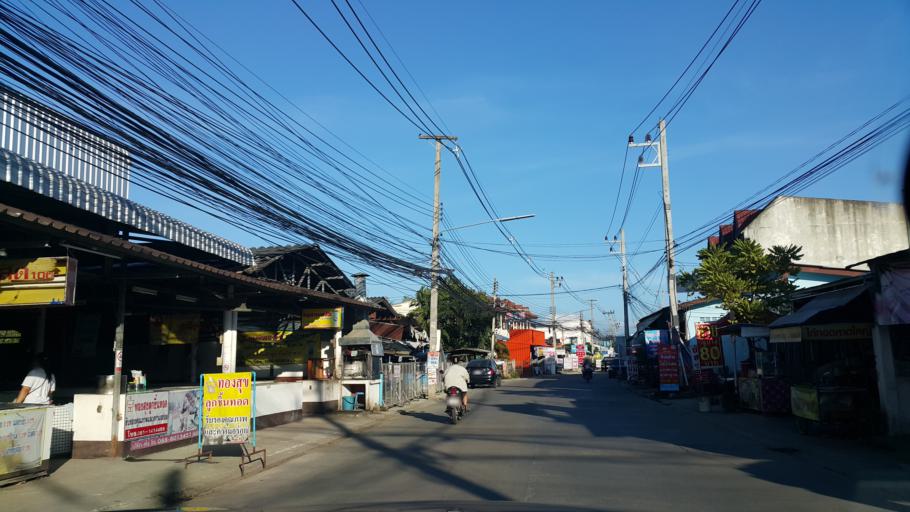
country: TH
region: Lamphun
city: Lamphun
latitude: 18.5997
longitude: 99.0254
